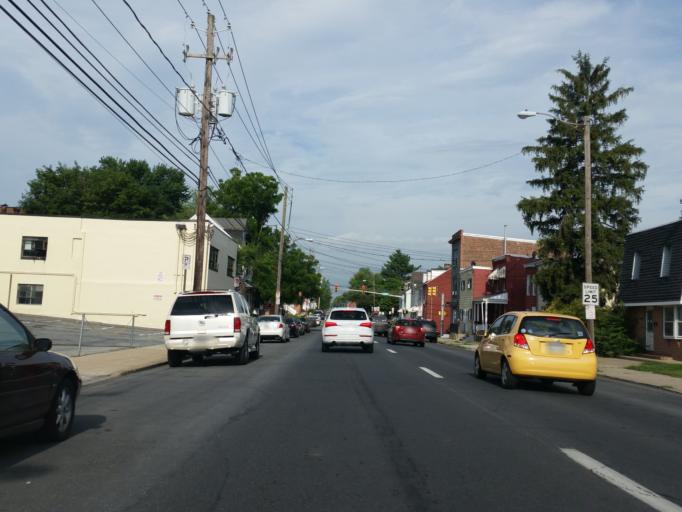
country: US
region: Pennsylvania
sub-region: Lancaster County
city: Lancaster
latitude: 40.0443
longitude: -76.2911
